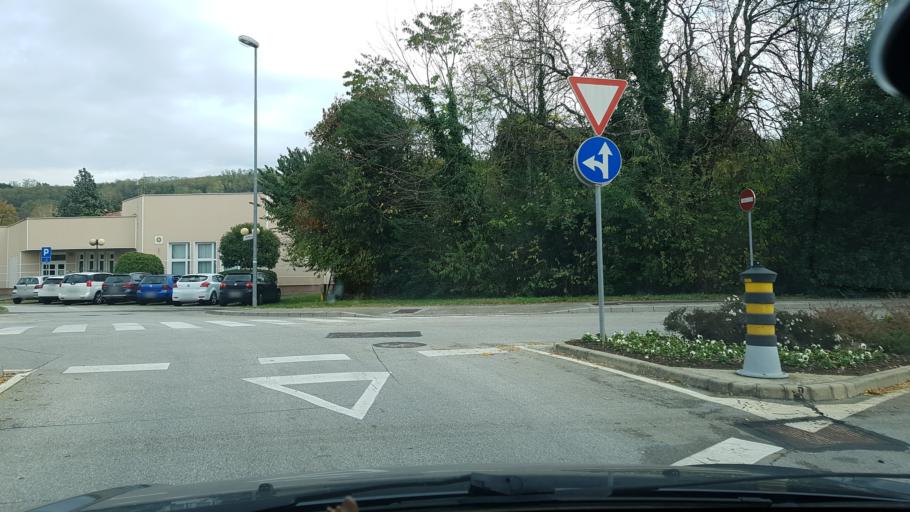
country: SI
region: Sempeter-Vrtojba
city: Sempeter pri Gorici
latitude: 45.9289
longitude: 13.6415
